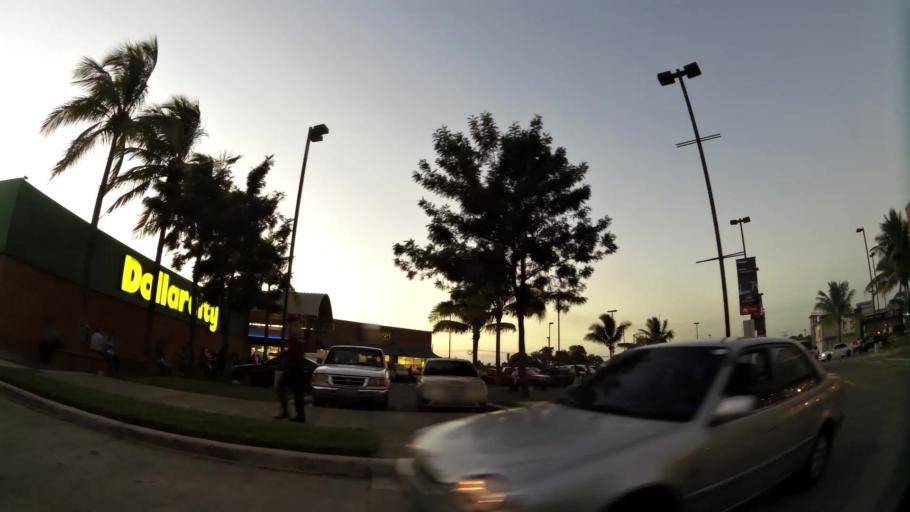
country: SV
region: La Libertad
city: Santa Tecla
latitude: 13.7290
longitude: -89.3594
